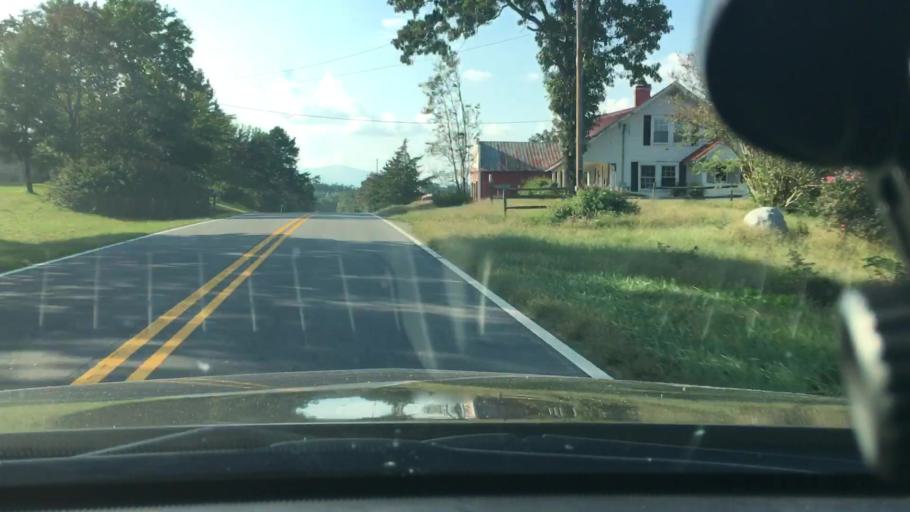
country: US
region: North Carolina
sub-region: Polk County
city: Columbus
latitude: 35.3224
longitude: -82.0993
